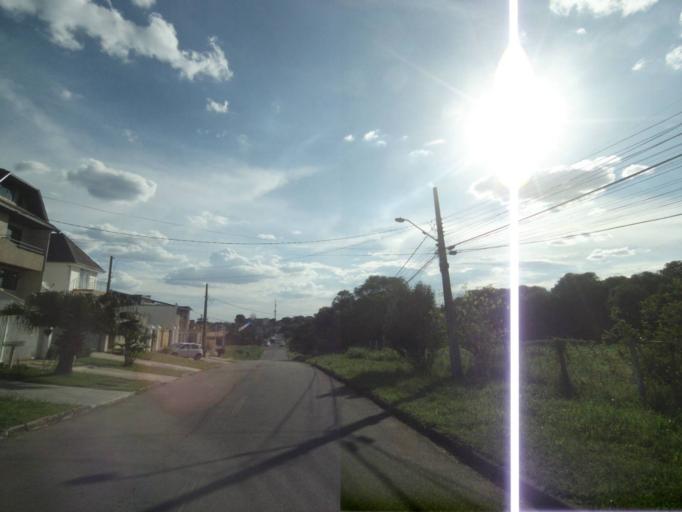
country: BR
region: Parana
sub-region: Pinhais
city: Pinhais
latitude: -25.4707
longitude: -49.2257
